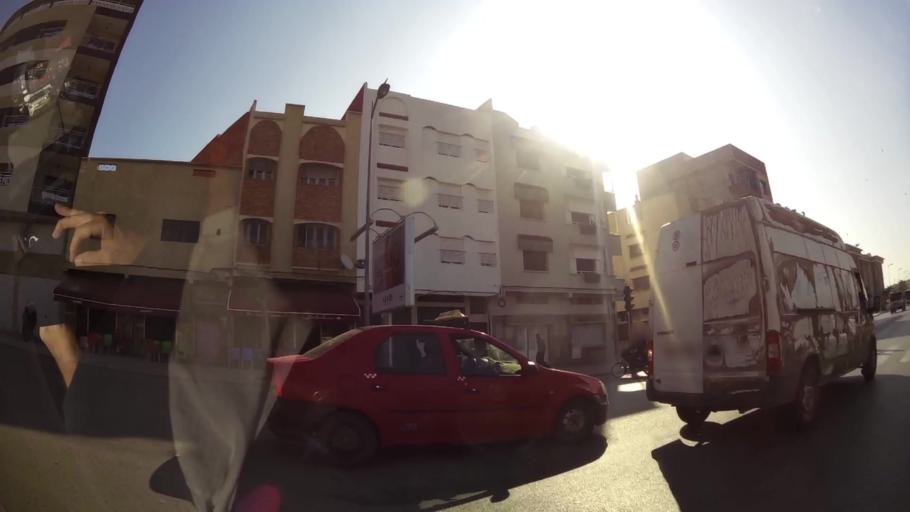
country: MA
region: Oriental
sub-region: Oujda-Angad
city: Oujda
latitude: 34.6794
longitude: -1.9319
